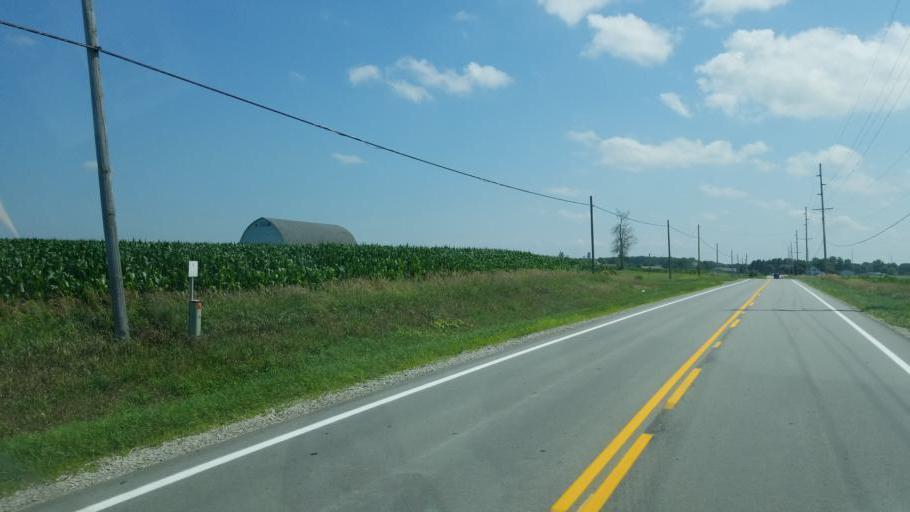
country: US
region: Ohio
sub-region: Huron County
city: Bellevue
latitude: 41.3093
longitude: -82.8294
